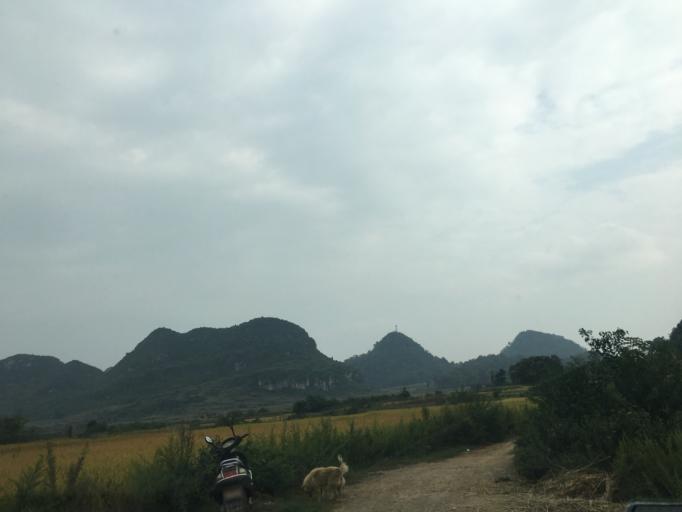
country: CN
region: Guangxi Zhuangzu Zizhiqu
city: Xinzhou
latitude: 25.4963
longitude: 105.6503
